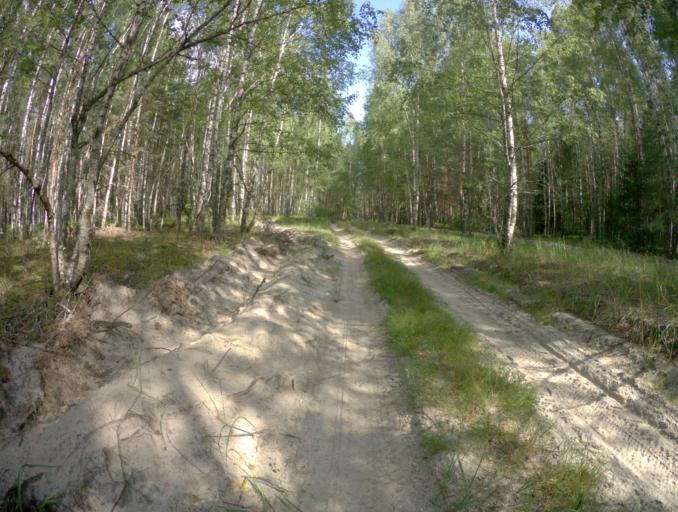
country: RU
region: Vladimir
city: Vorsha
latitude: 55.9091
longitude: 40.1648
